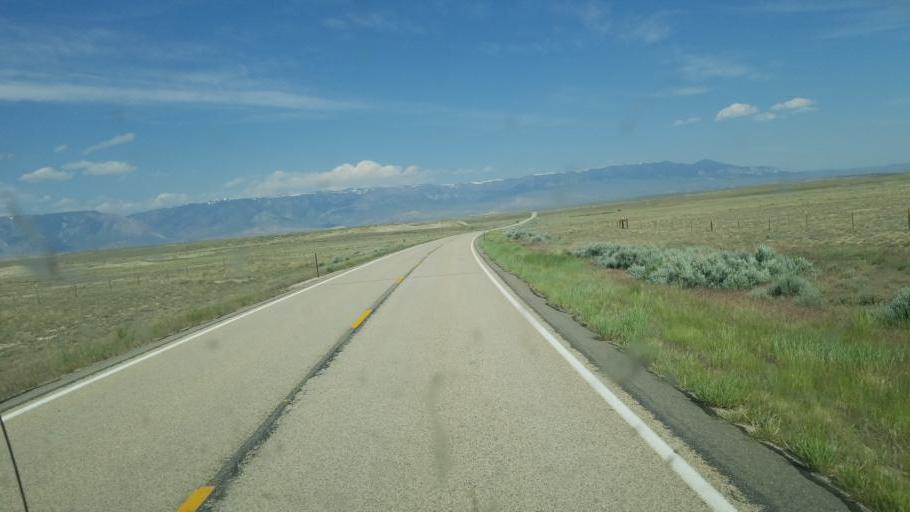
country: US
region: Wyoming
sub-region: Park County
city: Powell
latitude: 44.8481
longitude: -109.0053
